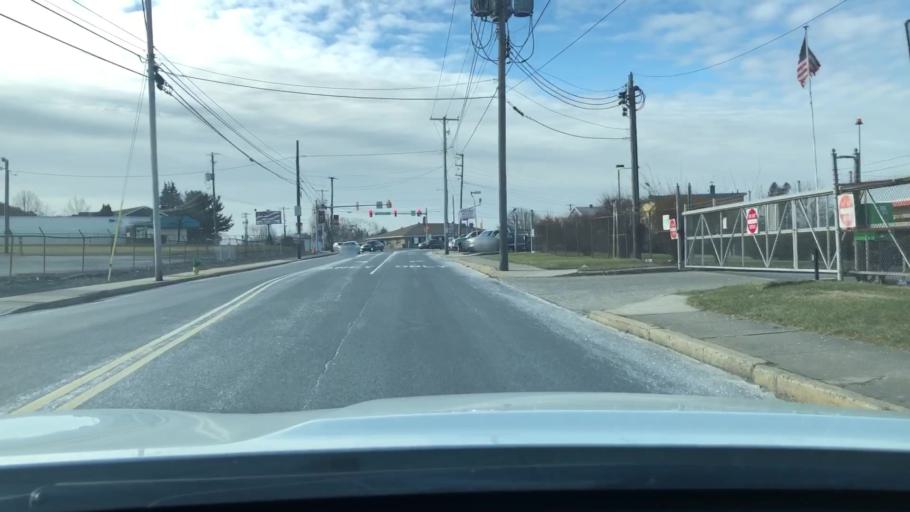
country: US
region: Pennsylvania
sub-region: Lehigh County
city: Catasauqua
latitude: 40.6444
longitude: -75.4825
